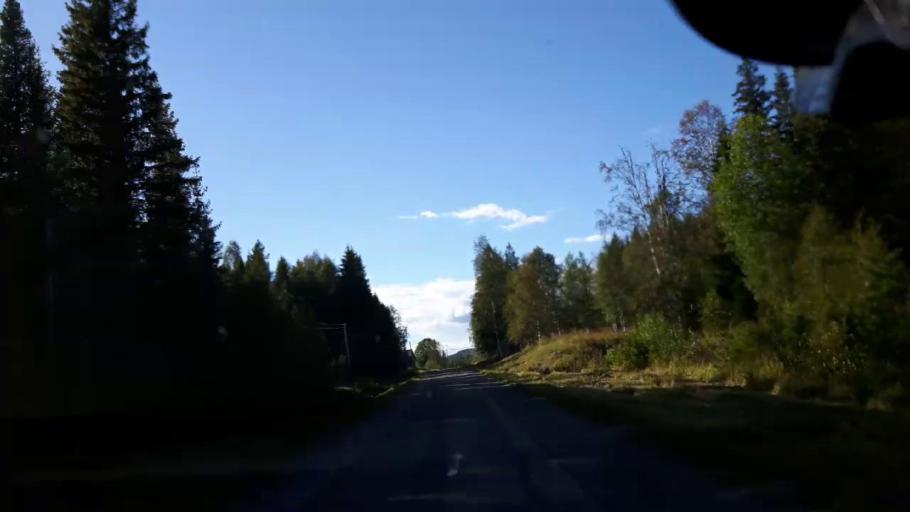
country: SE
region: Jaemtland
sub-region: Ragunda Kommun
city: Hammarstrand
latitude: 63.4913
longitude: 16.0488
